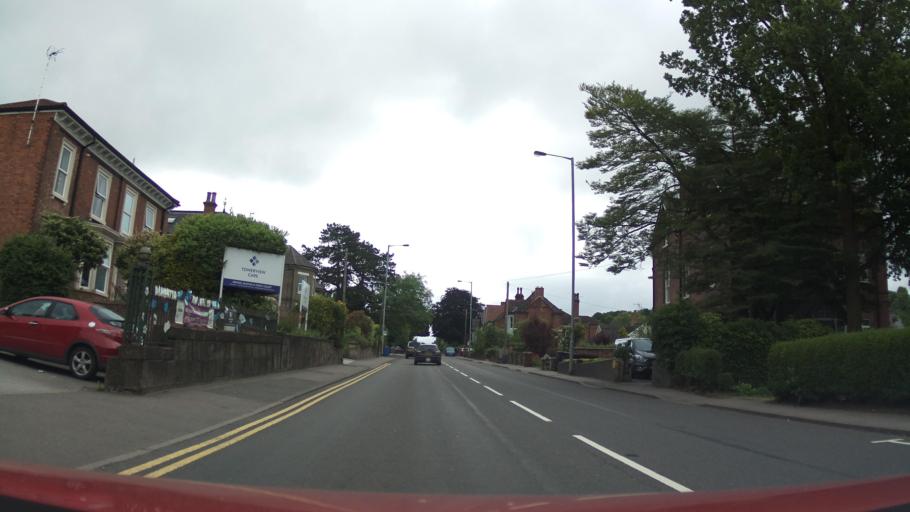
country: GB
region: England
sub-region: Staffordshire
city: Burton upon Trent
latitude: 52.8046
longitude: -1.6144
